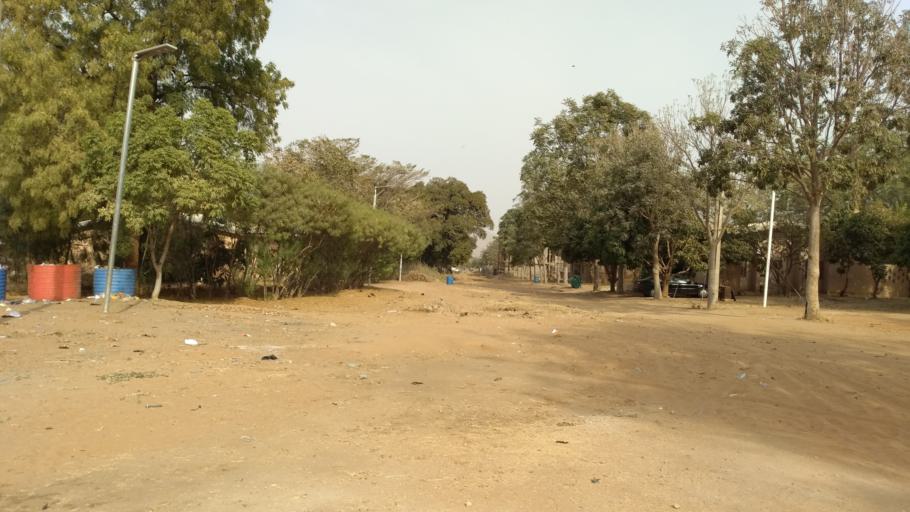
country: NG
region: Gombe
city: Gombe
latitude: 10.3077
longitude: 11.1731
